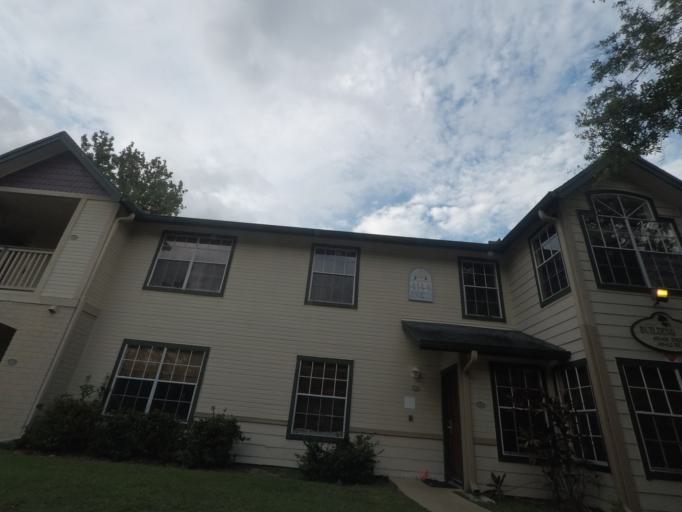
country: US
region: Florida
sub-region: Osceola County
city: Kissimmee
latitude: 28.3067
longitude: -81.4471
